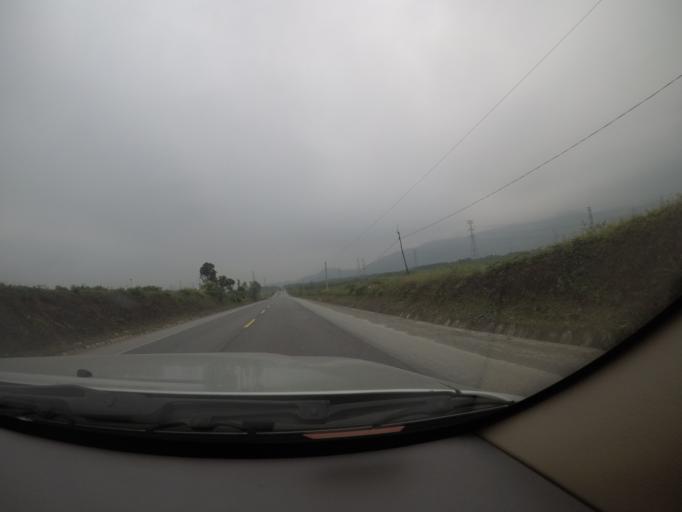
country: VN
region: Ha Tinh
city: Ky Anh
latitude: 18.0340
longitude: 106.3138
